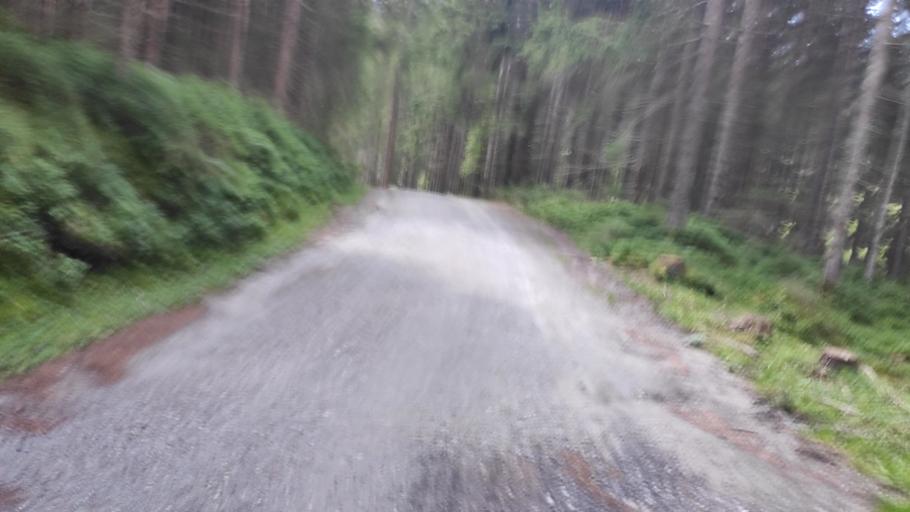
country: AT
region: Salzburg
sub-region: Politischer Bezirk Zell am See
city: Krimml
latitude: 47.2277
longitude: 12.1908
